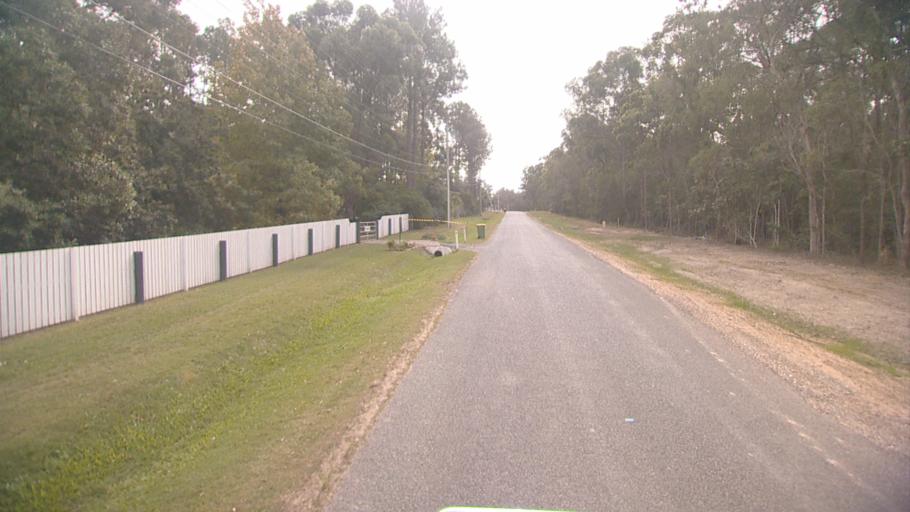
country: AU
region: Queensland
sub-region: Logan
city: Woodridge
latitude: -27.6624
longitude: 153.0669
